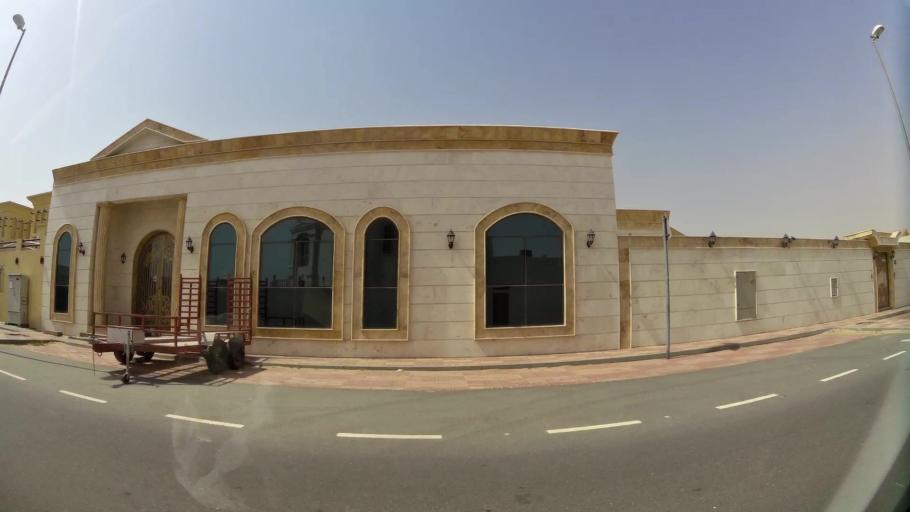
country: AE
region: Ash Shariqah
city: Sharjah
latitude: 25.2468
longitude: 55.4868
